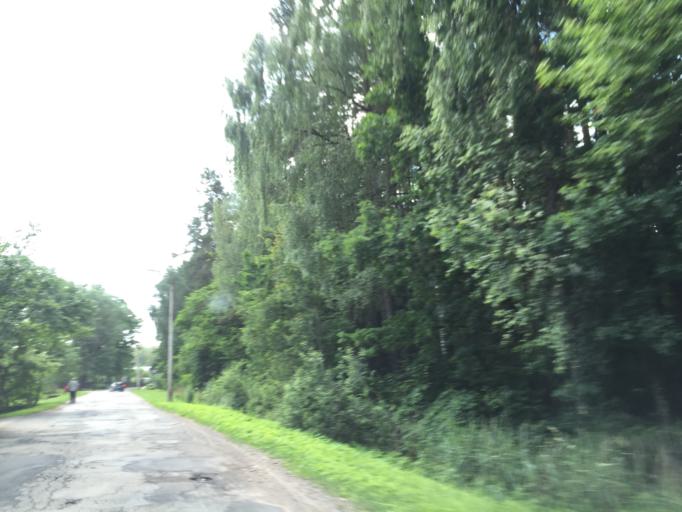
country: LV
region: Ozolnieku
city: Ozolnieki
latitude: 56.6911
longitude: 23.7637
